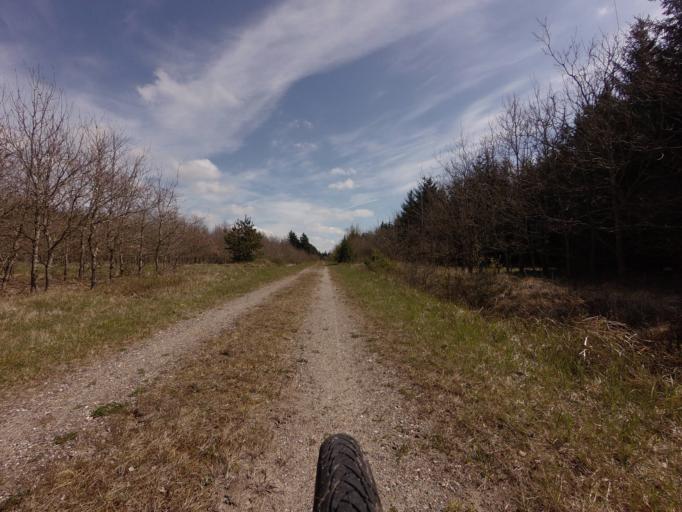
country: DK
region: North Denmark
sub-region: Jammerbugt Kommune
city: Brovst
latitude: 57.1696
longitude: 9.5641
